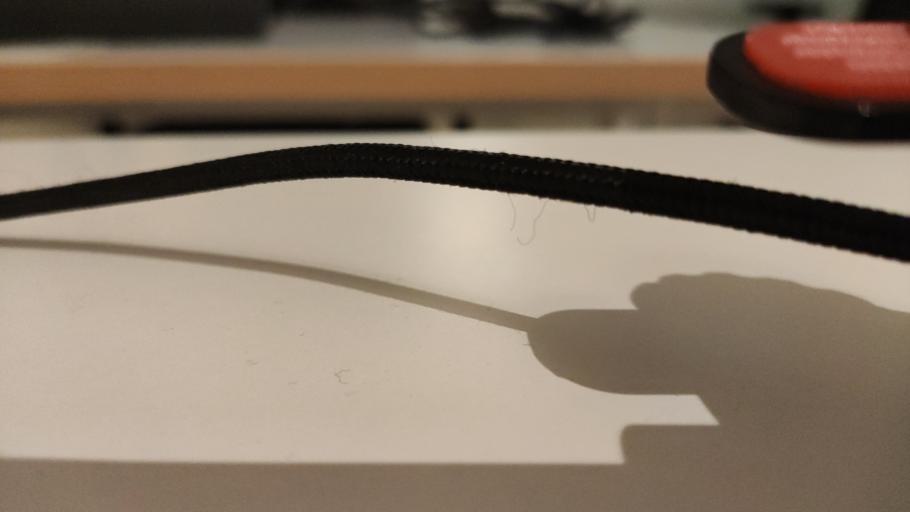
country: RU
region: Moskovskaya
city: Novoye
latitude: 55.6106
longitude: 38.9301
